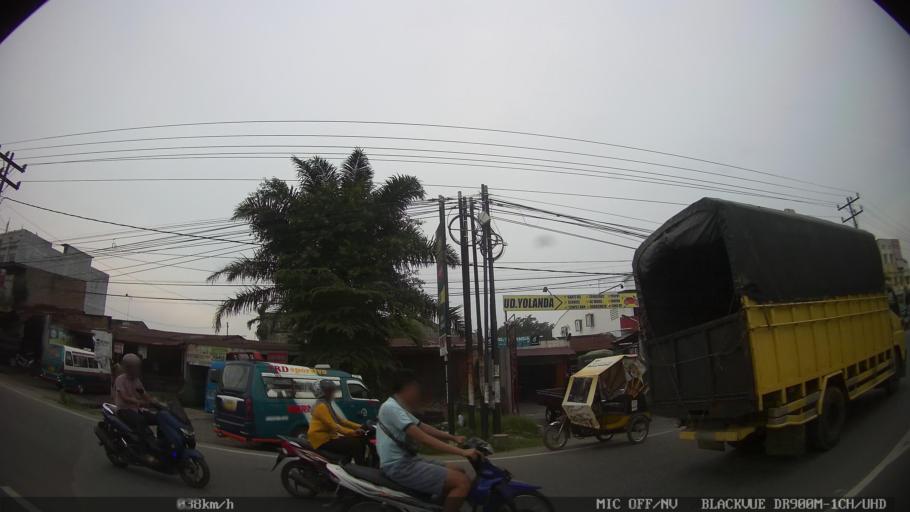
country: ID
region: North Sumatra
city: Deli Tua
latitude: 3.5401
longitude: 98.7173
